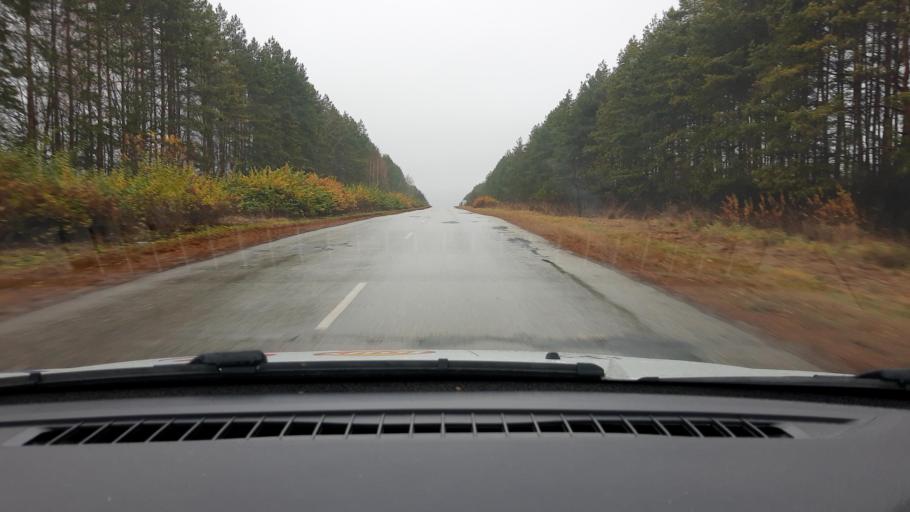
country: RU
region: Nizjnij Novgorod
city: Burevestnik
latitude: 56.0744
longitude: 43.9098
